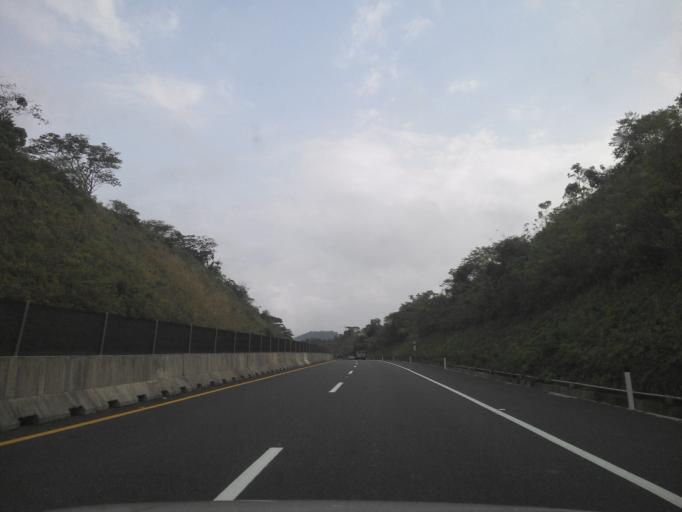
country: MX
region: Puebla
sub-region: Xicotepec
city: San Lorenzo
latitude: 20.4003
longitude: -97.9441
